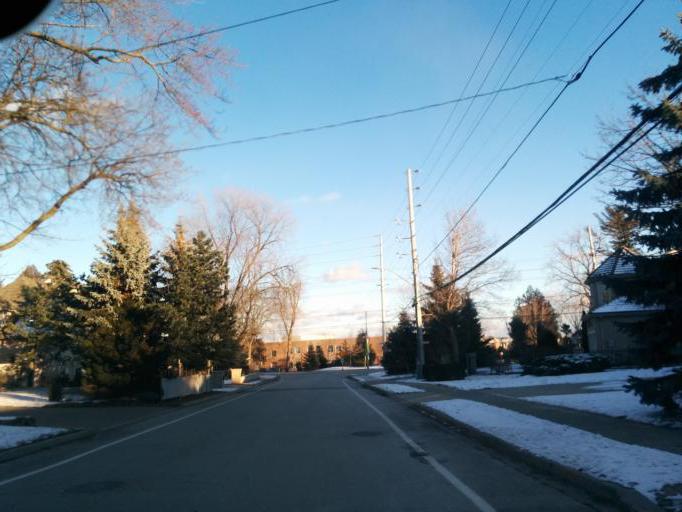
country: CA
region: Ontario
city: Mississauga
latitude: 43.5474
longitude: -79.6076
